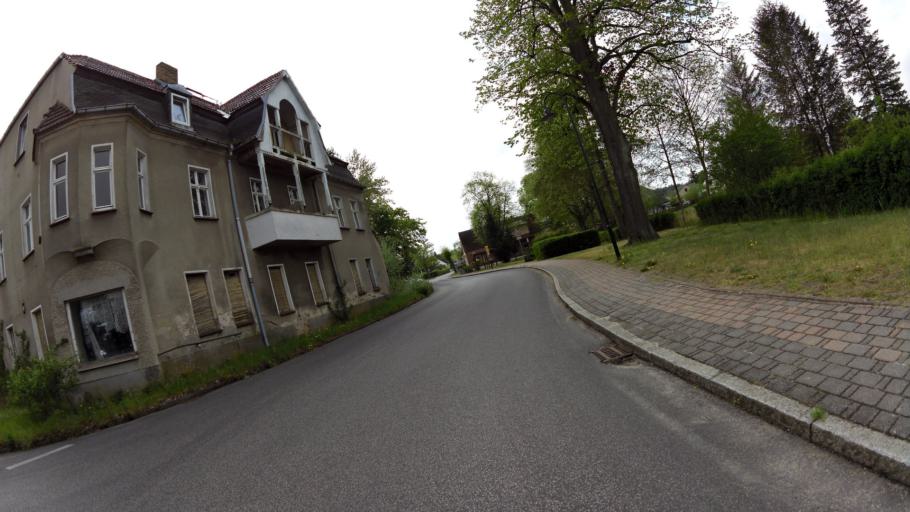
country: DE
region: Brandenburg
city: Bestensee
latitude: 52.2570
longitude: 13.7325
